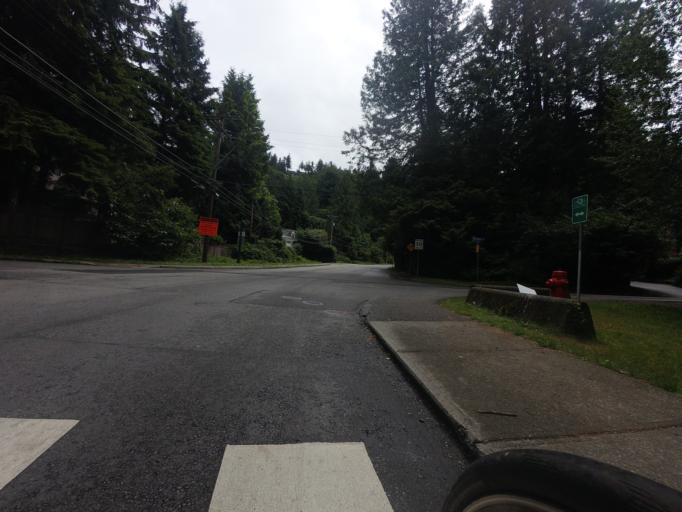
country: CA
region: British Columbia
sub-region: Greater Vancouver Regional District
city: Bowen Island
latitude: 49.3530
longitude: -123.2607
